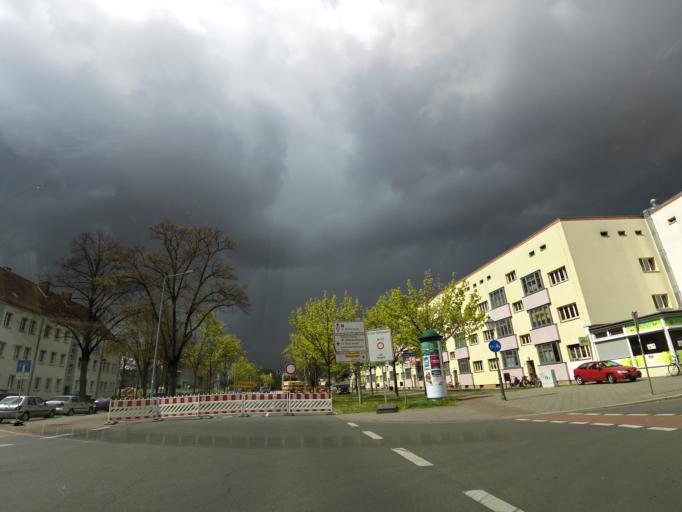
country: DE
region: Saxony-Anhalt
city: Magdeburg
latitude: 52.1293
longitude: 11.6695
